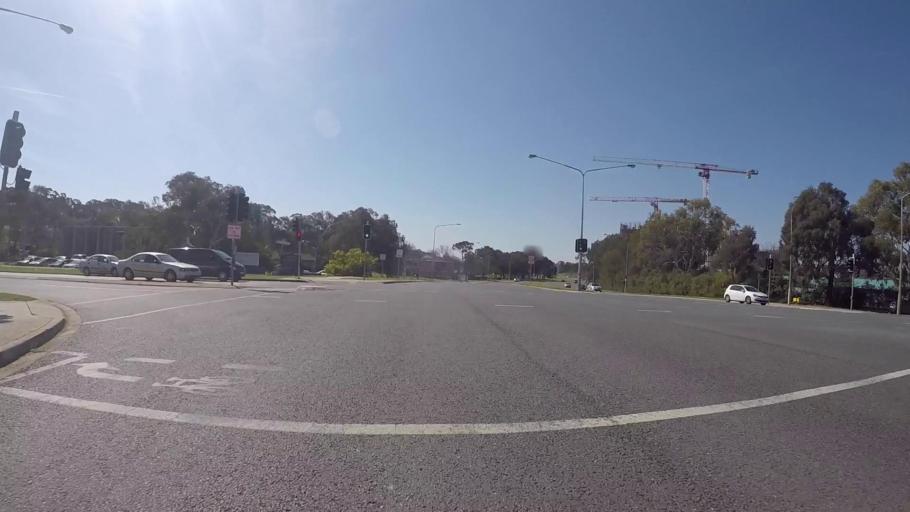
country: AU
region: Australian Capital Territory
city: Forrest
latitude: -35.3401
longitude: 149.0824
